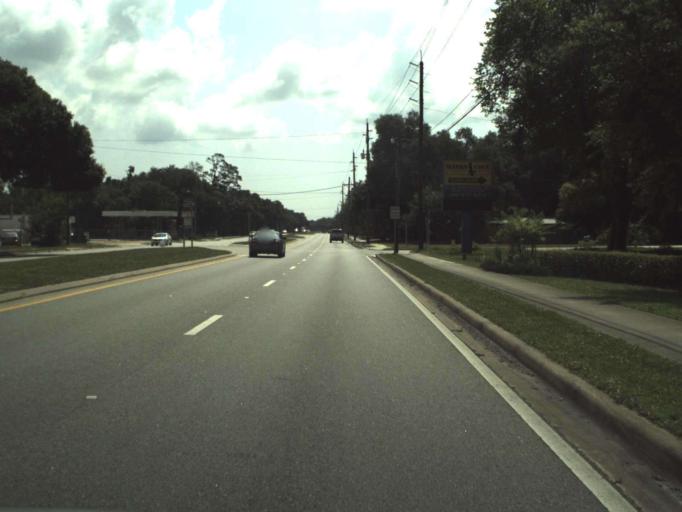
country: US
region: Florida
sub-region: Volusia County
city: Glencoe
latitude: 29.0133
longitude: -80.9566
